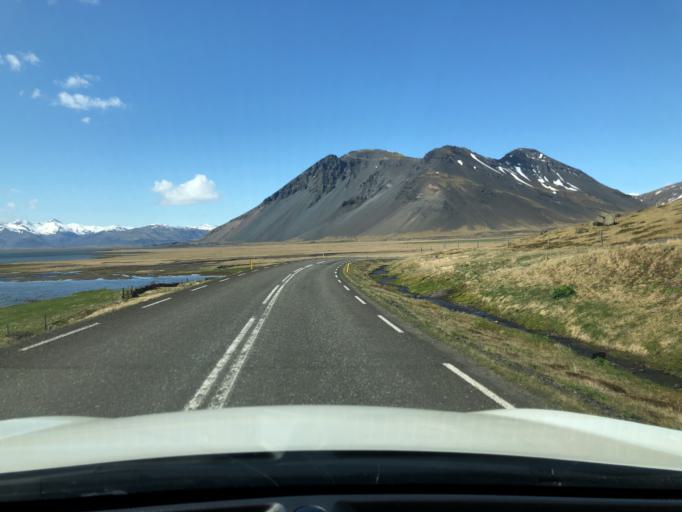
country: IS
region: East
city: Hoefn
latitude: 64.4283
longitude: -14.6269
